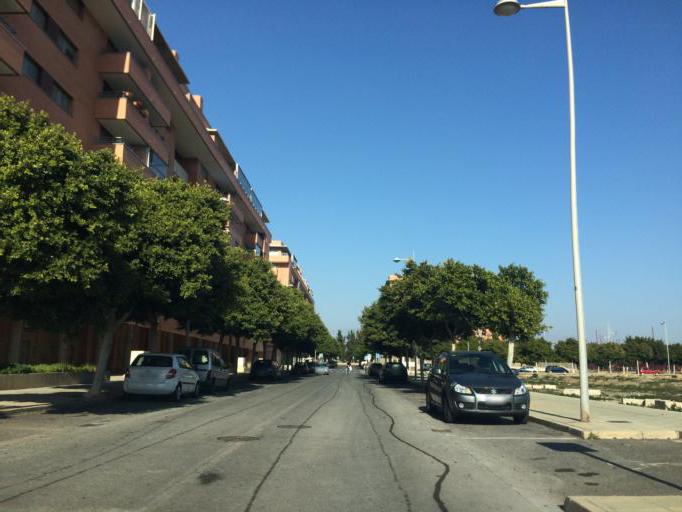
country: ES
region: Andalusia
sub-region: Provincia de Almeria
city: Almeria
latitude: 36.8356
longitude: -2.4334
